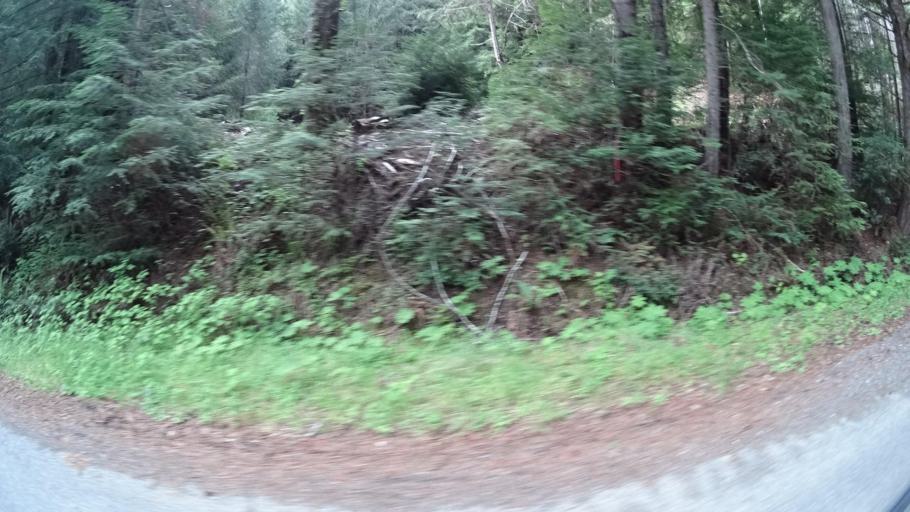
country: US
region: California
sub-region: Humboldt County
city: Redway
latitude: 40.3362
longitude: -123.8576
